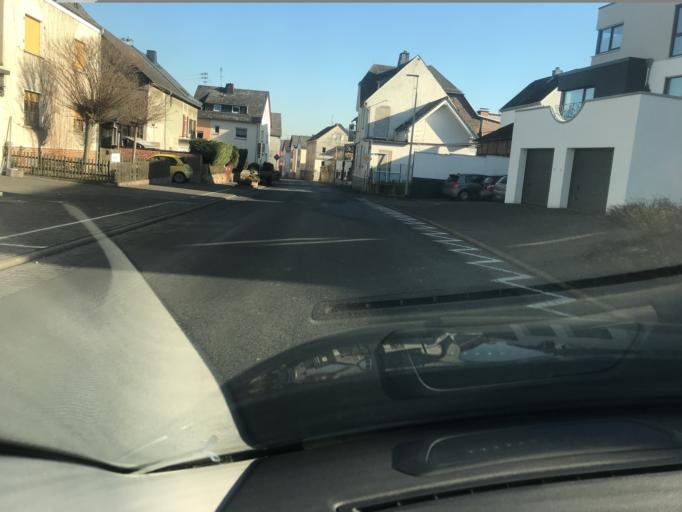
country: DE
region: Hesse
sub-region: Regierungsbezirk Giessen
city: Elz
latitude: 50.4107
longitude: 8.0288
